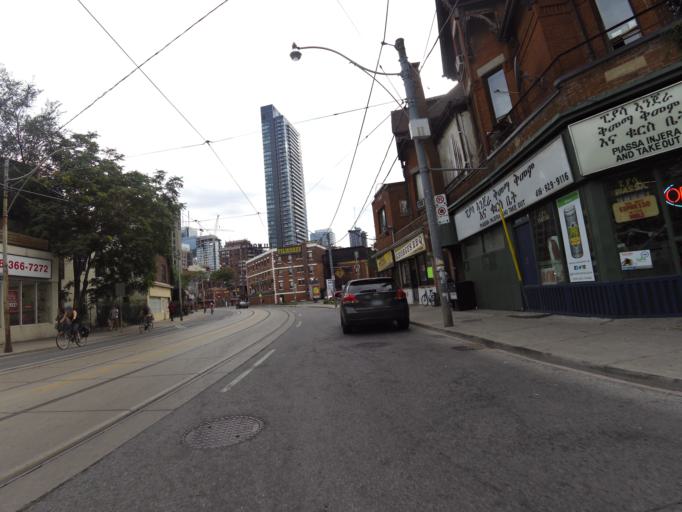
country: CA
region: Ontario
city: Toronto
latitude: 43.6582
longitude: -79.3724
